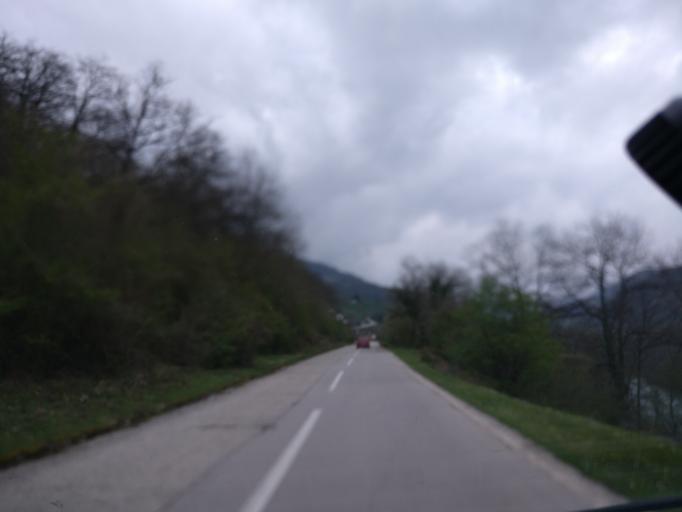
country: BA
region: Republika Srpska
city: Foca
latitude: 43.4425
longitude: 18.7593
